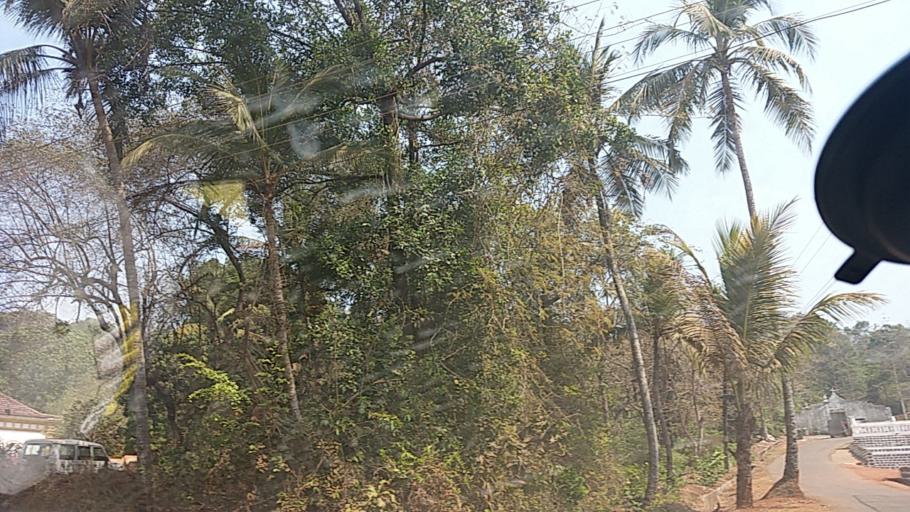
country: IN
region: Goa
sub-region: South Goa
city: Sancoale
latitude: 15.3736
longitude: 73.9153
